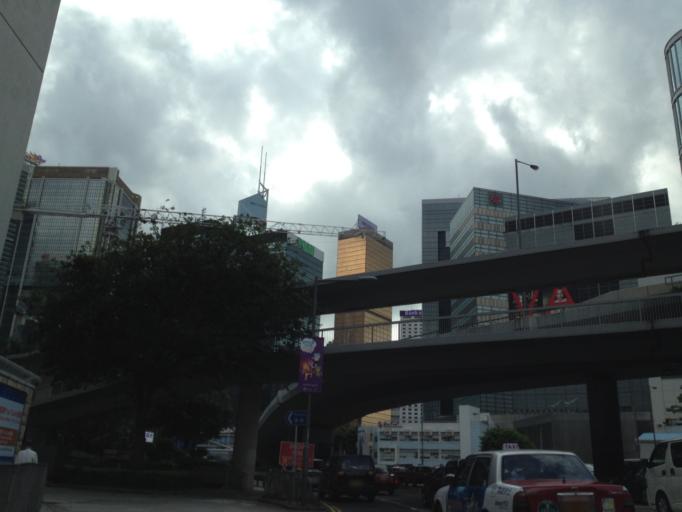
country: HK
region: Wanchai
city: Wan Chai
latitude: 22.2796
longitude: 114.1685
